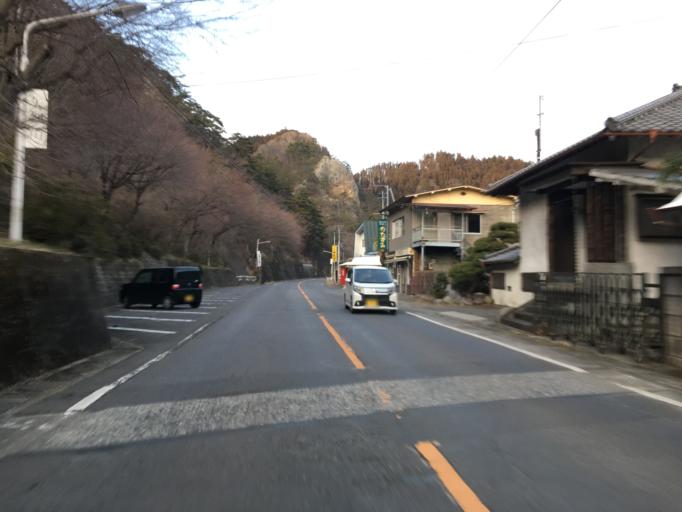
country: JP
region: Ibaraki
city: Daigo
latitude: 36.8515
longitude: 140.3971
